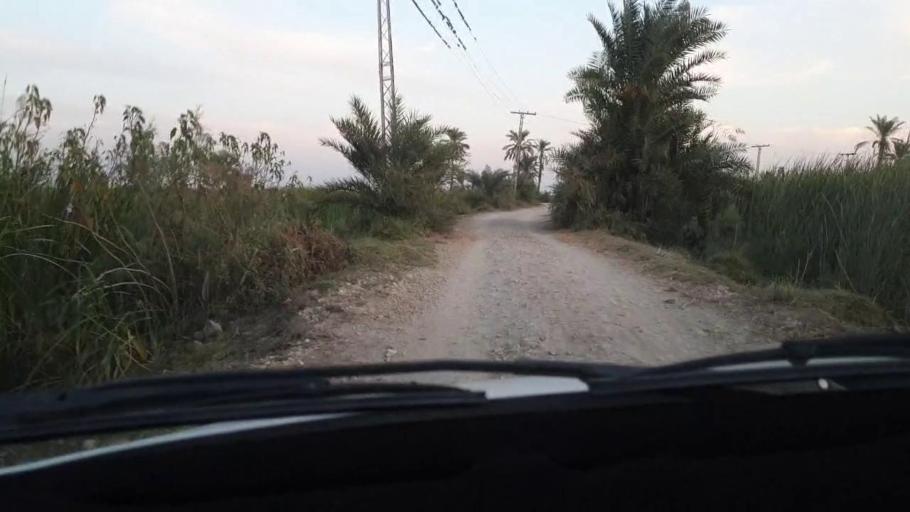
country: PK
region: Sindh
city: Tando Muhammad Khan
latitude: 25.0920
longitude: 68.3928
